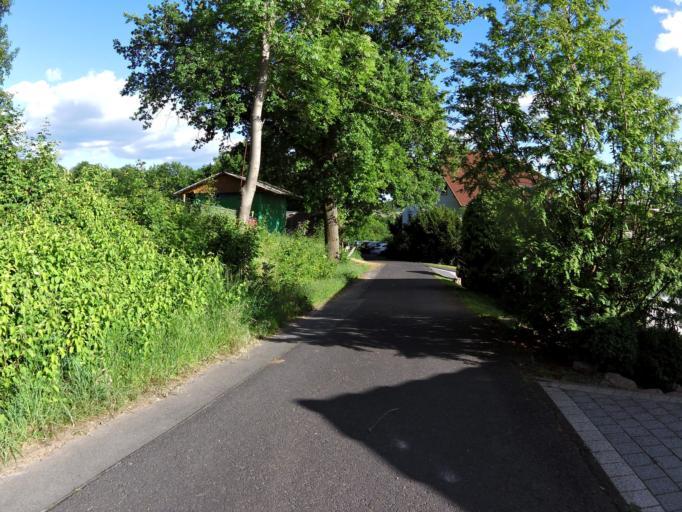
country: DE
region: Hesse
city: Philippsthal
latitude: 50.8384
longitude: 10.0156
